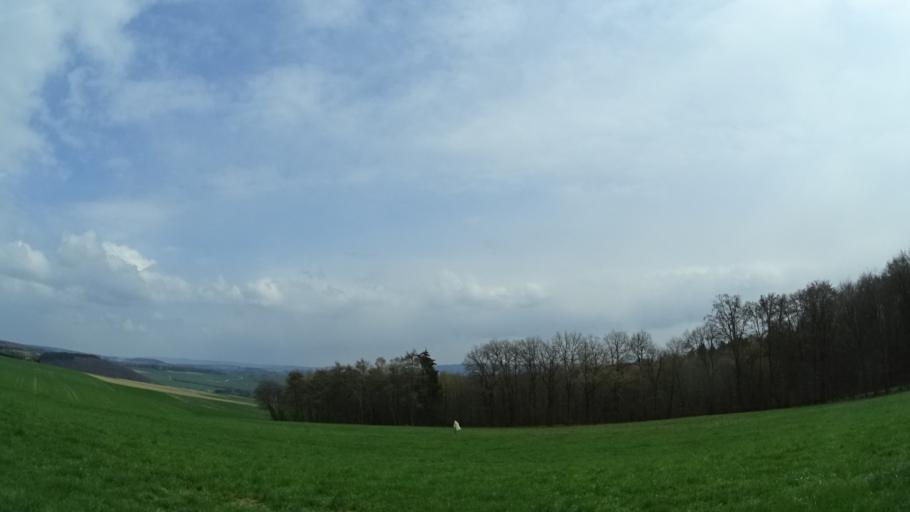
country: DE
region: Rheinland-Pfalz
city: Weitersbach
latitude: 49.8668
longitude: 7.3074
